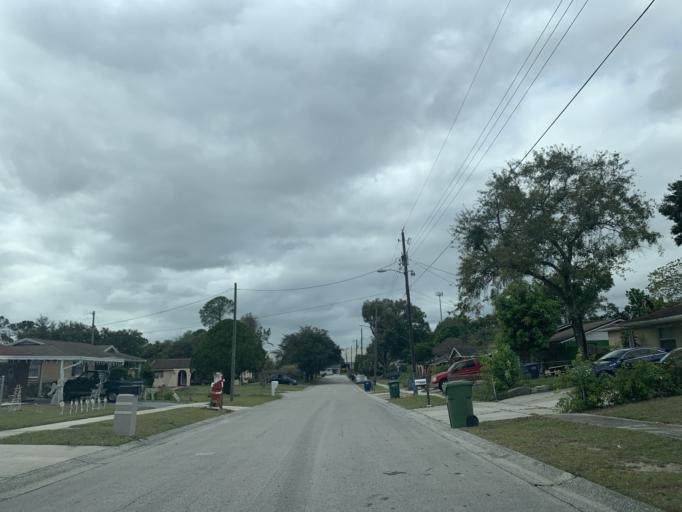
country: US
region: Florida
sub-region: Hillsborough County
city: East Lake-Orient Park
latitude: 27.9885
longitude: -82.4034
